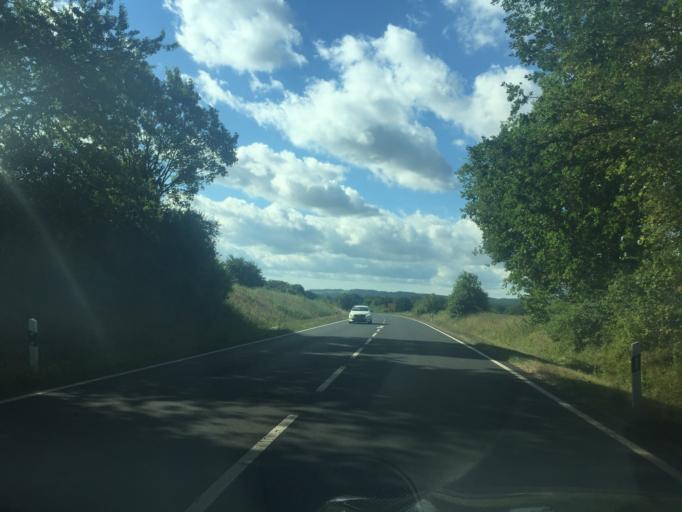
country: DE
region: Bavaria
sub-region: Upper Palatinate
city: Hahnbach
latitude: 49.5261
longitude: 11.8116
